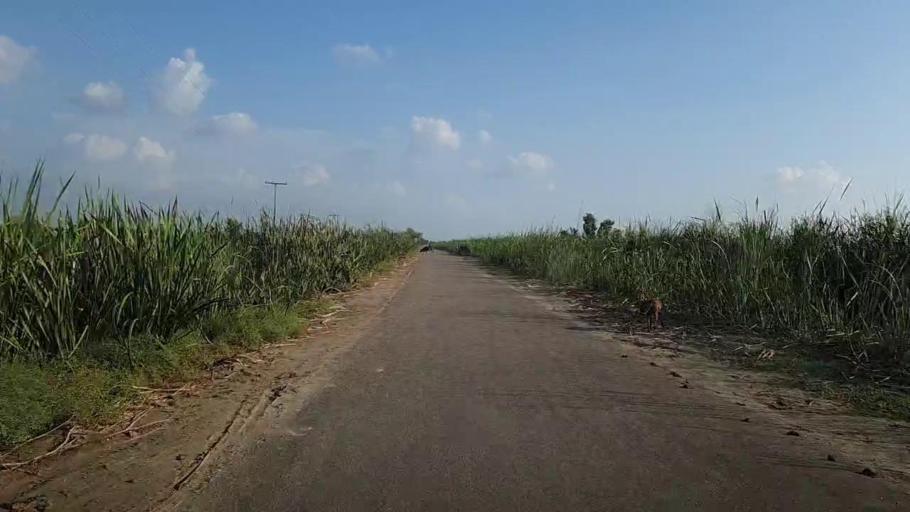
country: PK
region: Sindh
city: Hingorja
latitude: 27.0959
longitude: 68.4024
